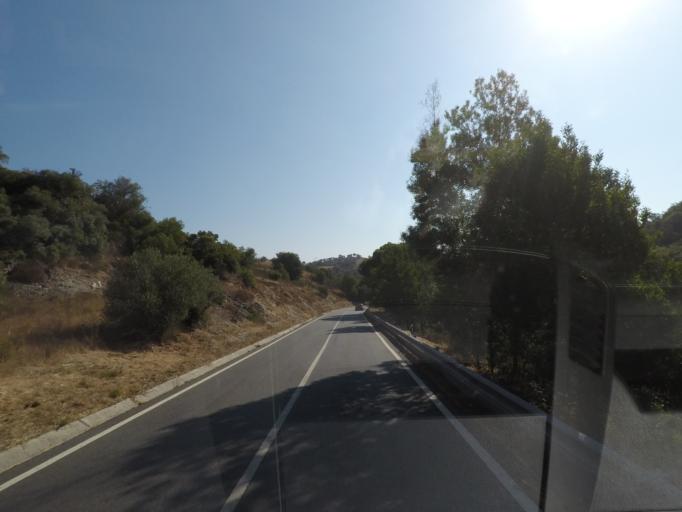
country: PT
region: Beja
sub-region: Odemira
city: Odemira
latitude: 37.6112
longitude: -8.7160
